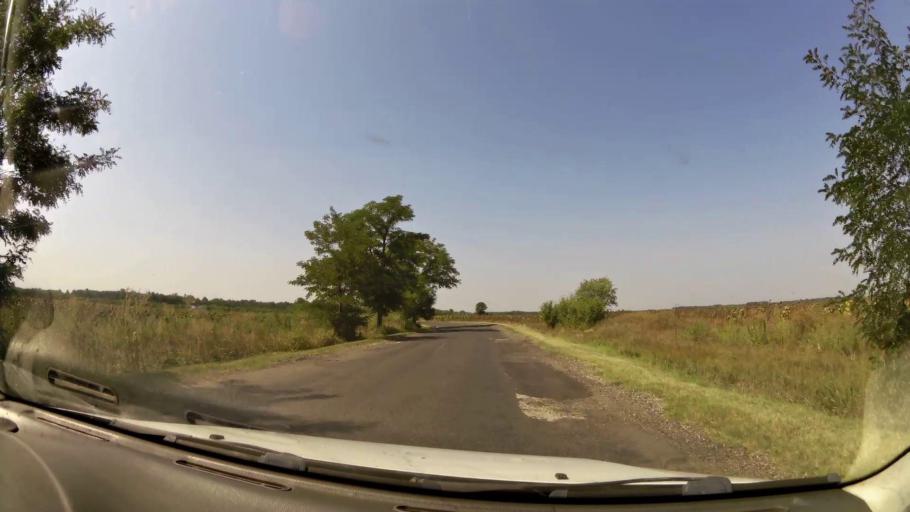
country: HU
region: Pest
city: Tapioszolos
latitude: 47.3211
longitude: 19.8581
